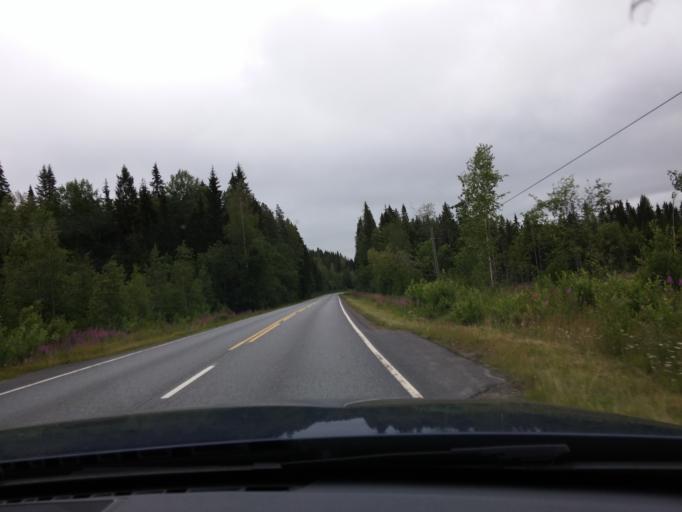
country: FI
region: Central Finland
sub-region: Joutsa
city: Luhanka
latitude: 61.8251
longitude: 25.9114
